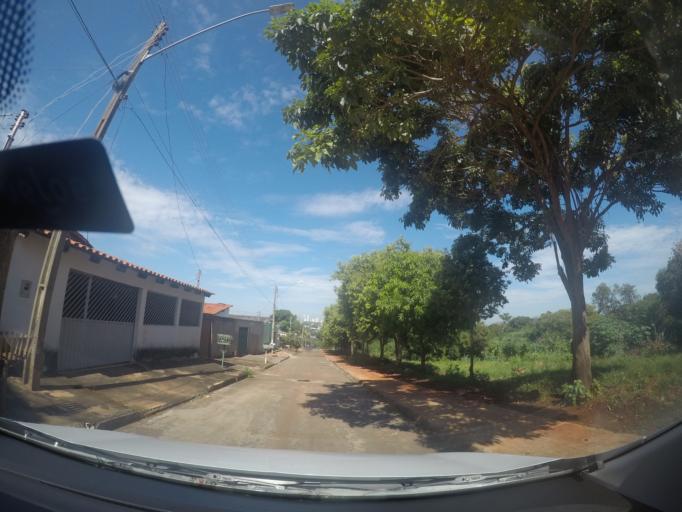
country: BR
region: Goias
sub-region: Goiania
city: Goiania
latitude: -16.6654
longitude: -49.1928
